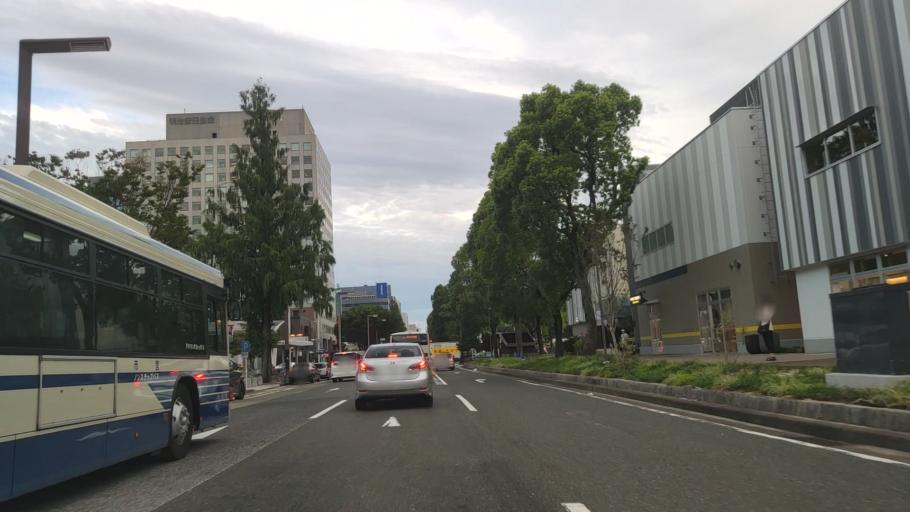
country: JP
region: Aichi
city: Nagoya-shi
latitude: 35.1711
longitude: 136.9089
